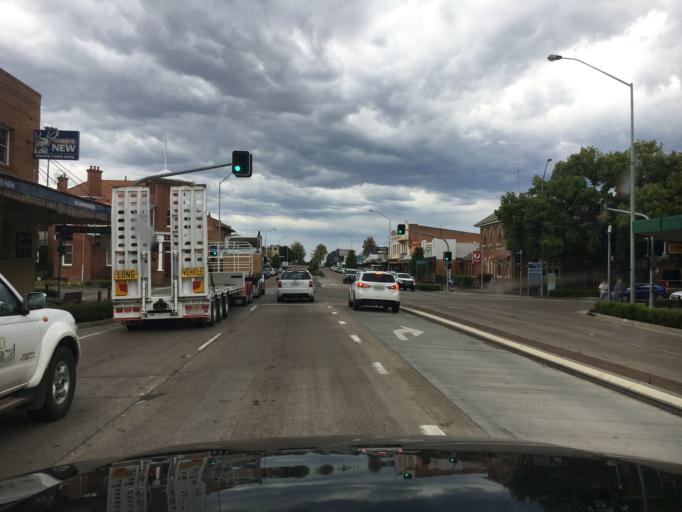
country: AU
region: New South Wales
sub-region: Muswellbrook
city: Muswellbrook
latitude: -32.0502
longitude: 150.8677
